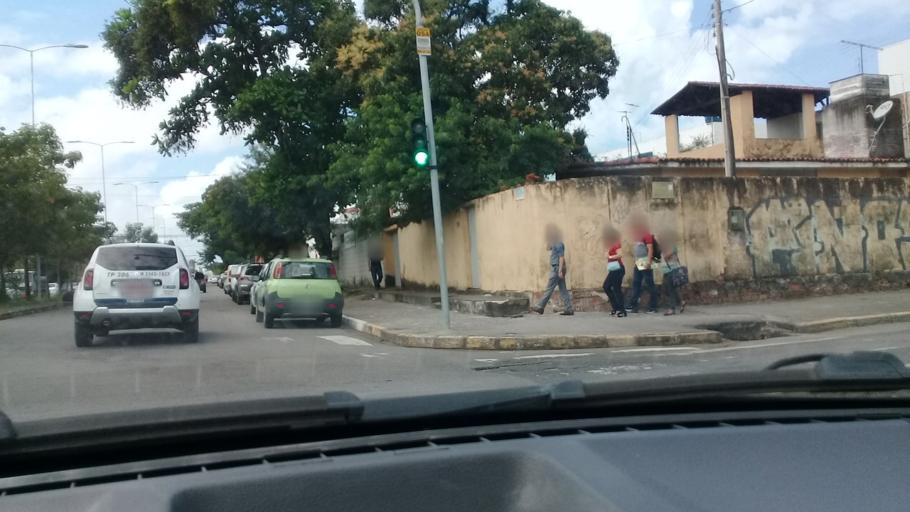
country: BR
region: Pernambuco
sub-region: Jaboatao Dos Guararapes
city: Jaboatao
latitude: -8.1642
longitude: -34.9192
